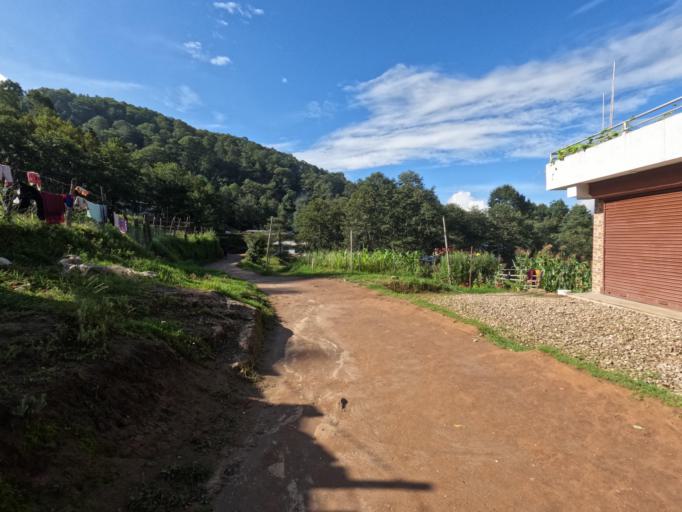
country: NP
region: Eastern Region
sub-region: Sagarmatha Zone
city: Namche Bazar
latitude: 27.4948
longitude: 86.5836
